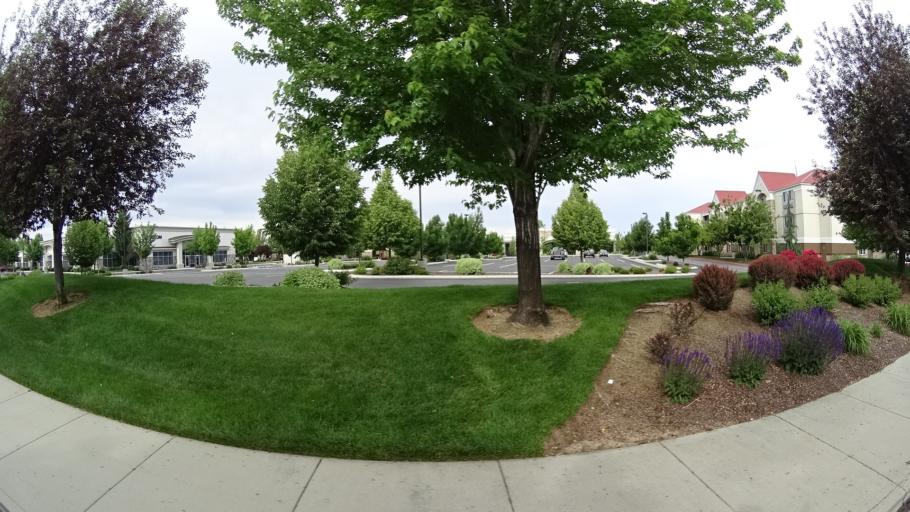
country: US
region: Idaho
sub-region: Ada County
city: Meridian
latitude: 43.5874
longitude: -116.3519
